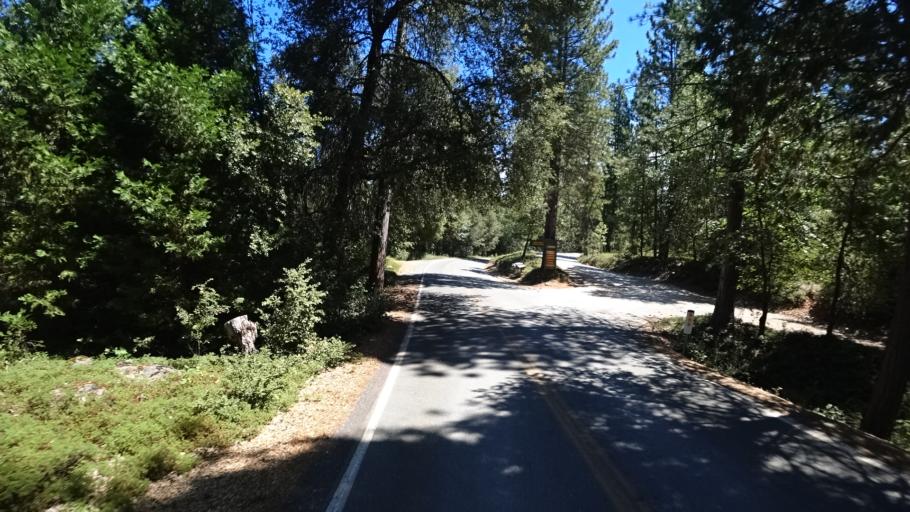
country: US
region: California
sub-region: Amador County
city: Pioneer
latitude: 38.3552
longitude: -120.5378
